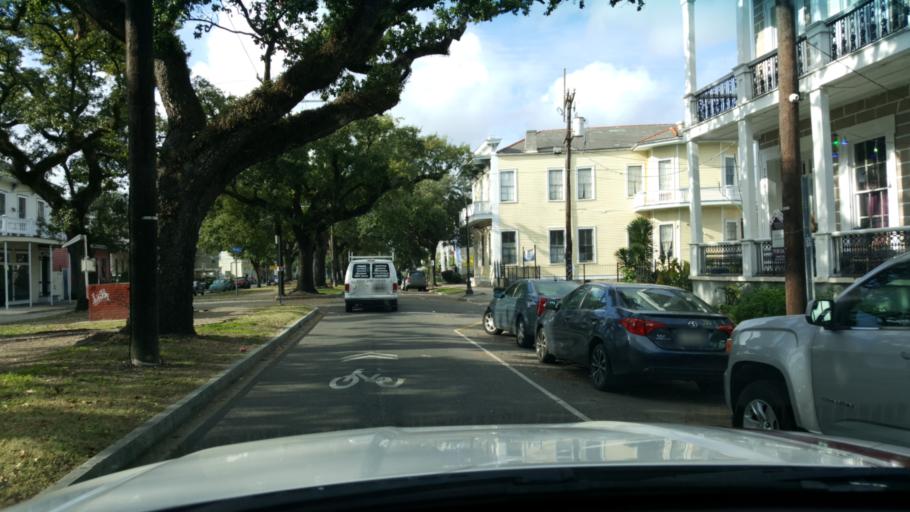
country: US
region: Louisiana
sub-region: Orleans Parish
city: New Orleans
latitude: 29.9673
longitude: -90.0656
